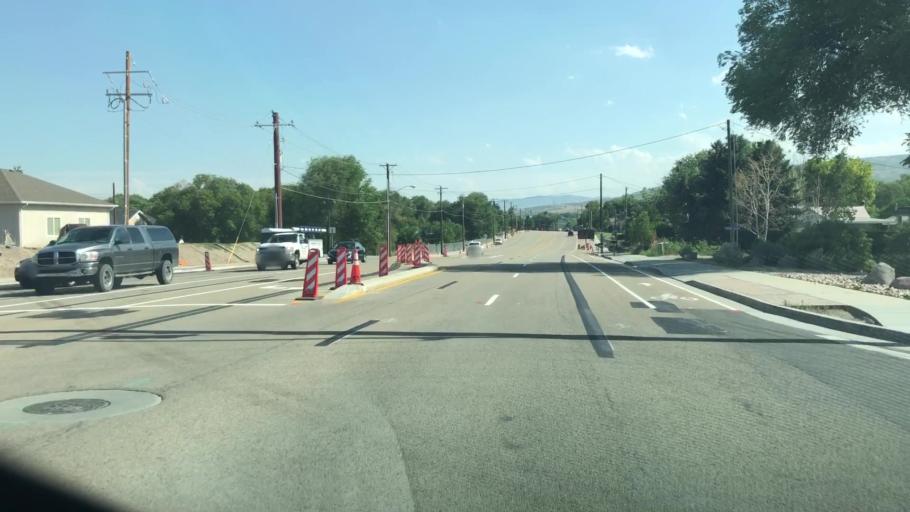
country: US
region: Utah
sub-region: Salt Lake County
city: Bluffdale
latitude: 40.4973
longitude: -111.9387
